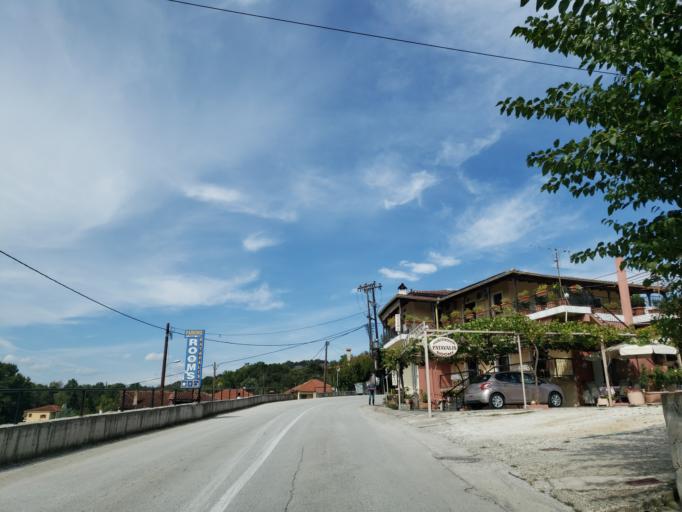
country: GR
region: Thessaly
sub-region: Trikala
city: Kastraki
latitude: 39.7179
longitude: 21.6168
